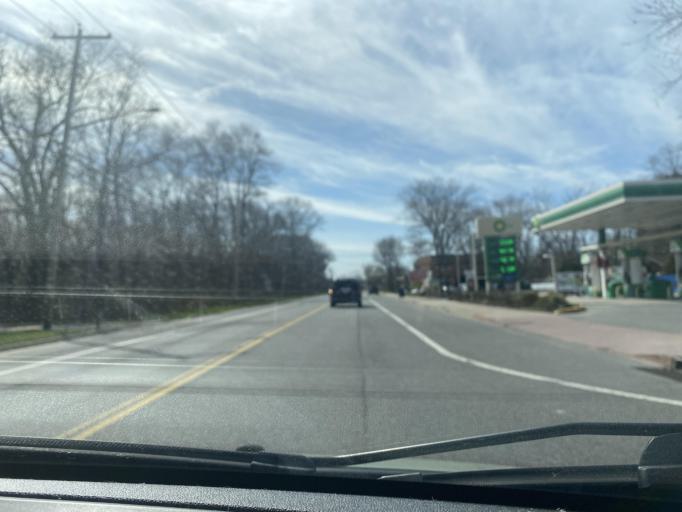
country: US
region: New York
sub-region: Suffolk County
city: Rocky Point
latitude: 40.9479
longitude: -72.9114
